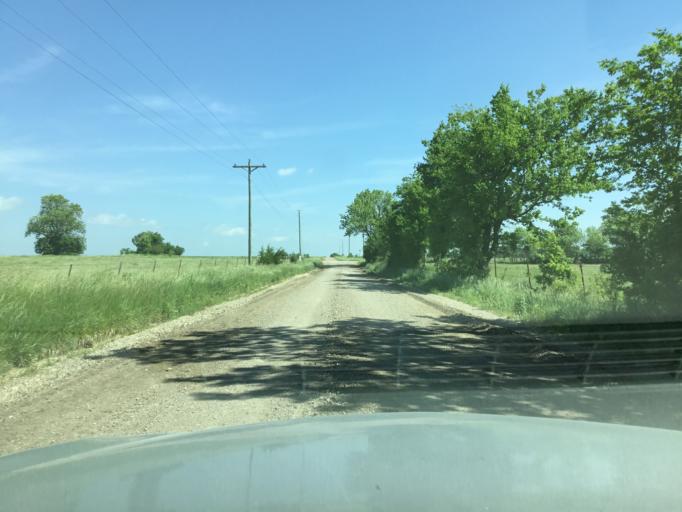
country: US
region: Kansas
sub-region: Labette County
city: Oswego
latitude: 37.1777
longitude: -95.1399
